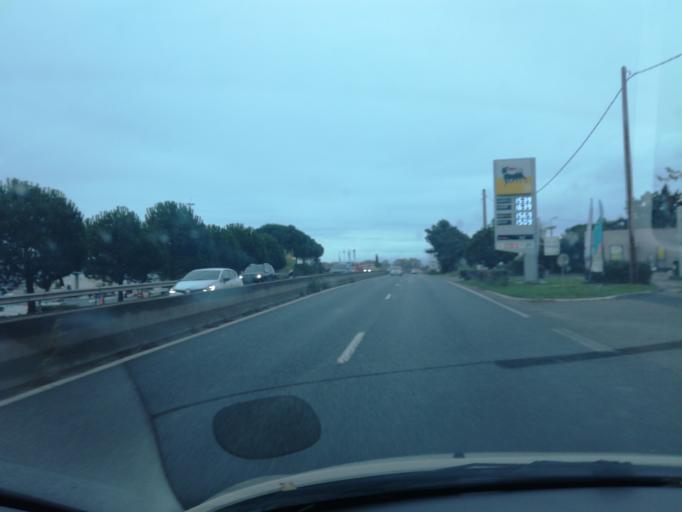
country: FR
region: Provence-Alpes-Cote d'Azur
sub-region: Departement du Var
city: Puget-sur-Argens
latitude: 43.4425
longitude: 6.7036
